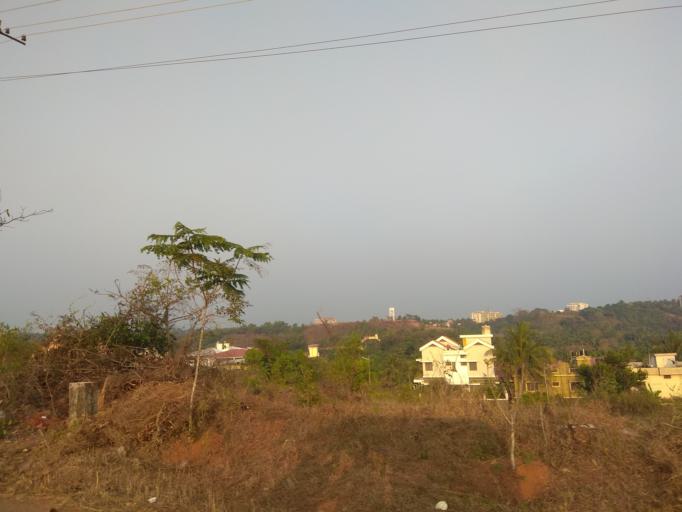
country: IN
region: Karnataka
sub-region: Dakshina Kannada
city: Mangalore
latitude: 12.9150
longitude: 74.8594
